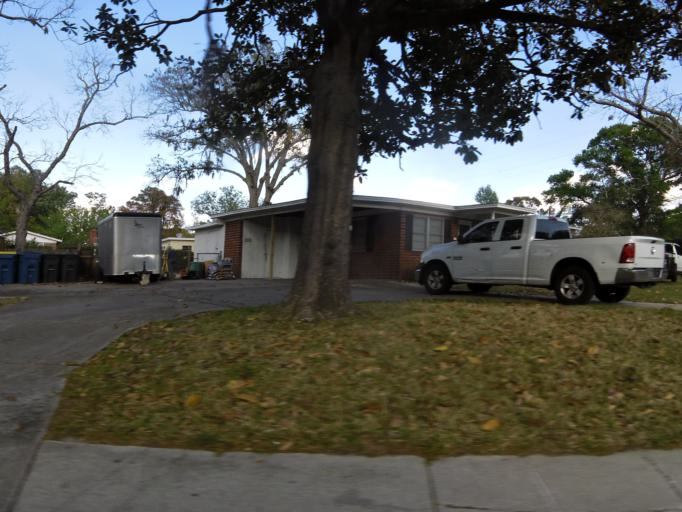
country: US
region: Florida
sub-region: Duval County
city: Jacksonville
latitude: 30.3455
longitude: -81.5976
